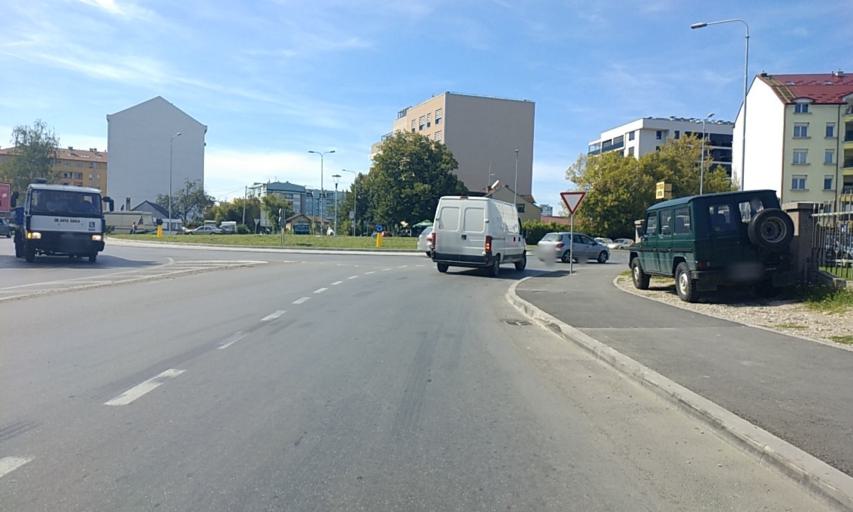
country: BA
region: Republika Srpska
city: Starcevica
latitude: 44.7664
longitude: 17.2098
